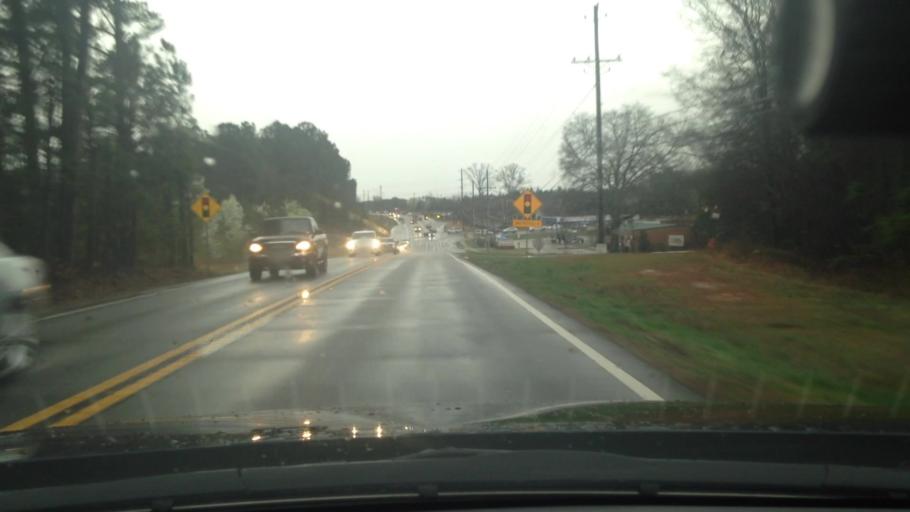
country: US
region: Georgia
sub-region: Fayette County
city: Peachtree City
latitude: 33.3837
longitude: -84.6727
